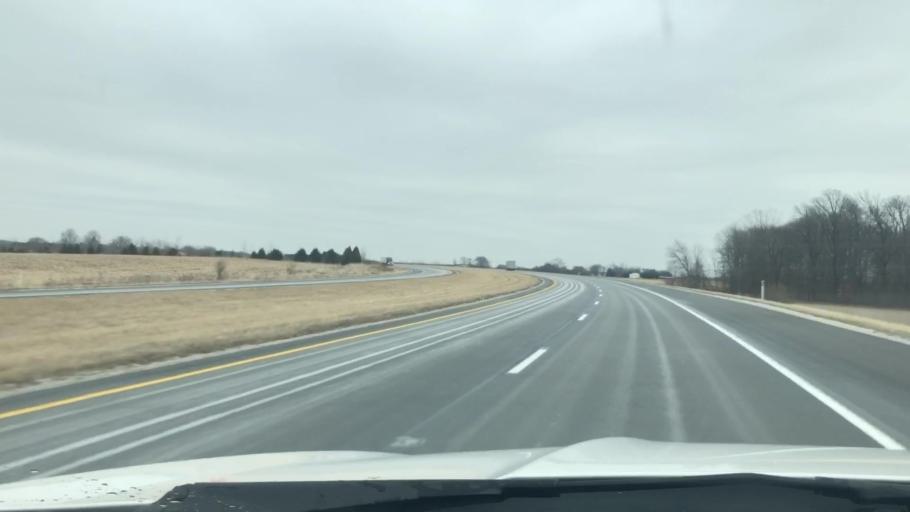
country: US
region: Indiana
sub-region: Cass County
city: Walton
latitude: 40.7366
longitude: -86.2714
